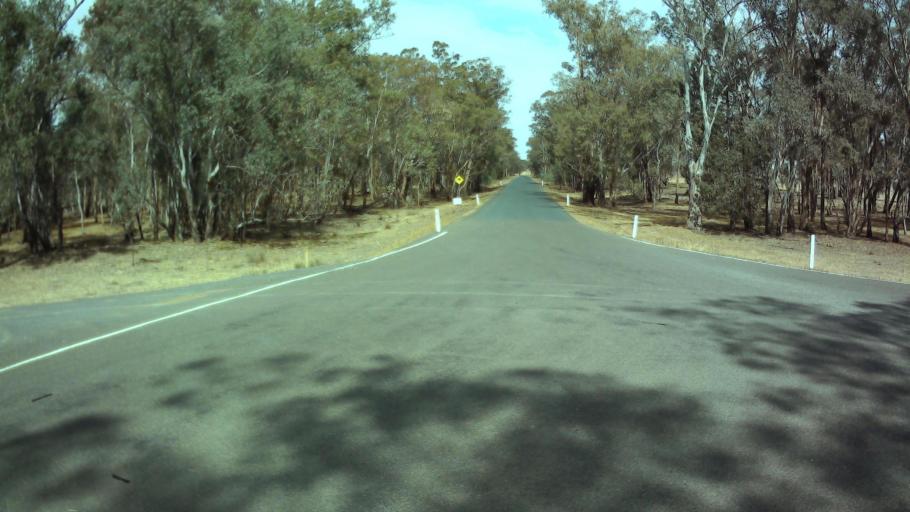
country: AU
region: New South Wales
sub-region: Weddin
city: Grenfell
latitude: -33.8085
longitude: 148.0763
